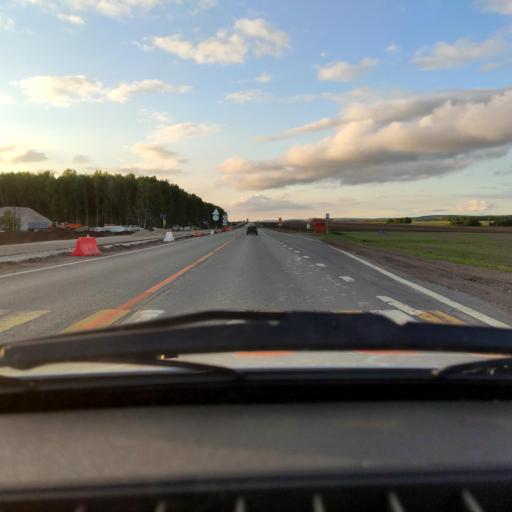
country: RU
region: Bashkortostan
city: Tolbazy
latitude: 54.1297
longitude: 55.9020
